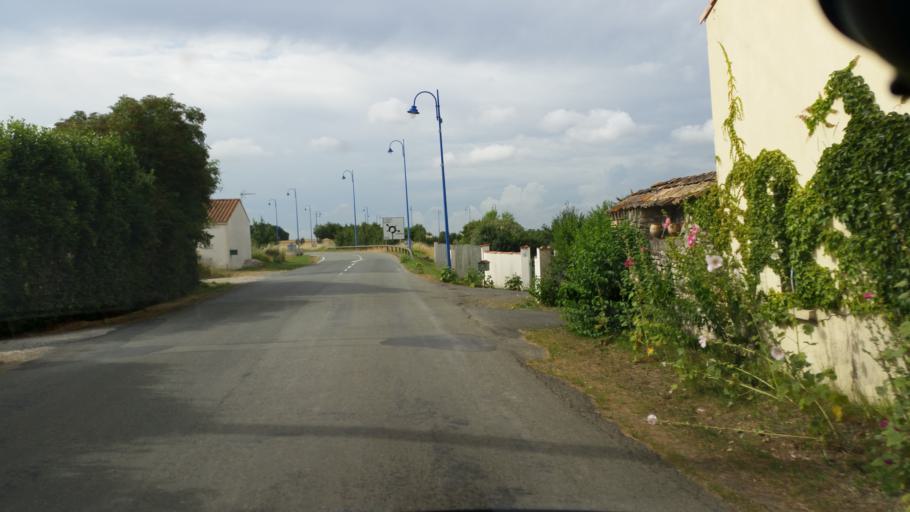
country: FR
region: Poitou-Charentes
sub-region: Departement de la Charente-Maritime
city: Courcon
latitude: 46.1936
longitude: -0.8672
